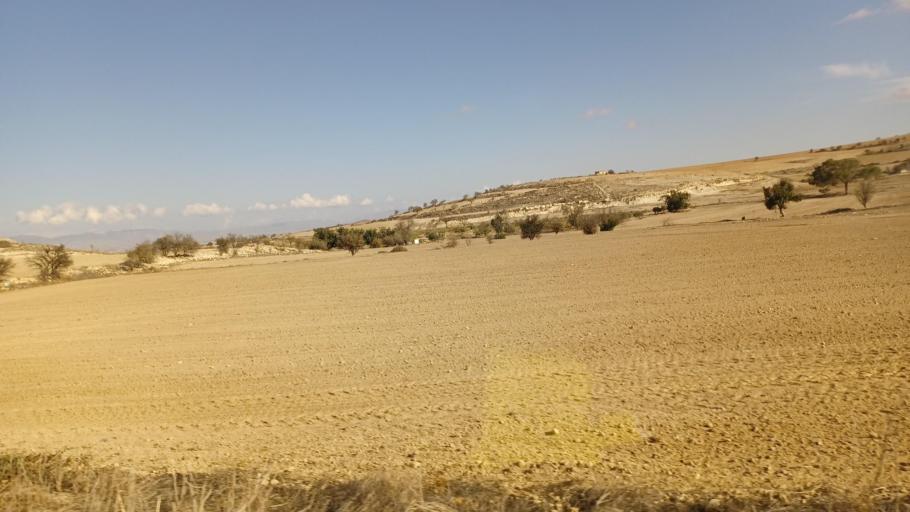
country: CY
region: Larnaka
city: Athienou
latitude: 35.0358
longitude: 33.5710
